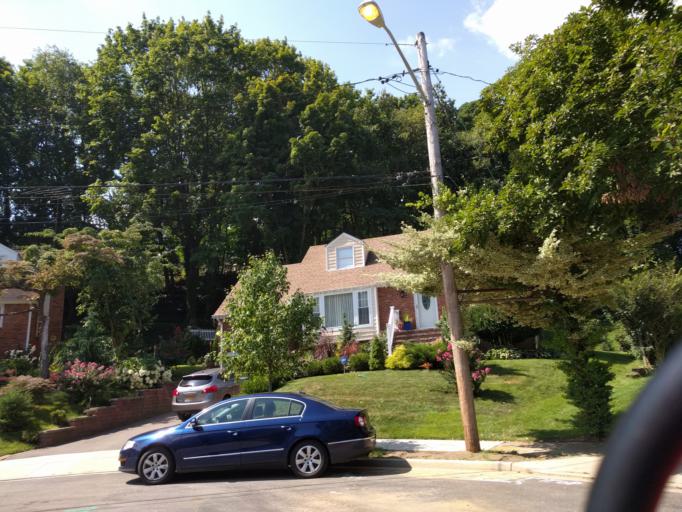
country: US
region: New York
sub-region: Nassau County
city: Oyster Bay
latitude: 40.8632
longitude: -73.5318
